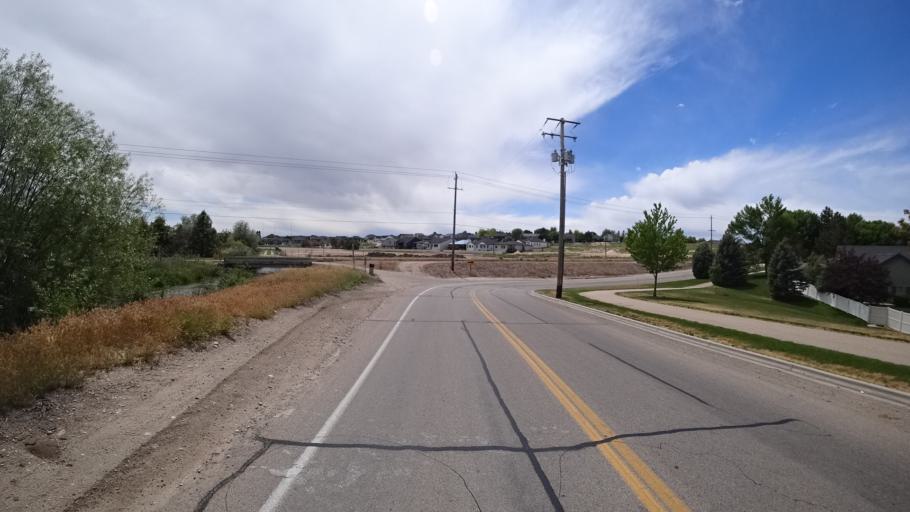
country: US
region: Idaho
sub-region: Ada County
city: Meridian
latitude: 43.5759
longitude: -116.3990
